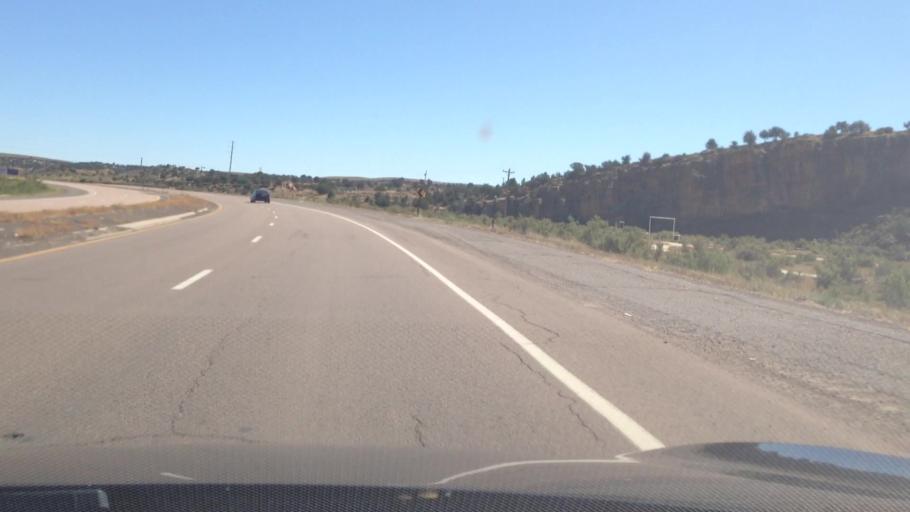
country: US
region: Arizona
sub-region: Apache County
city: Window Rock
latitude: 35.6508
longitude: -109.0384
